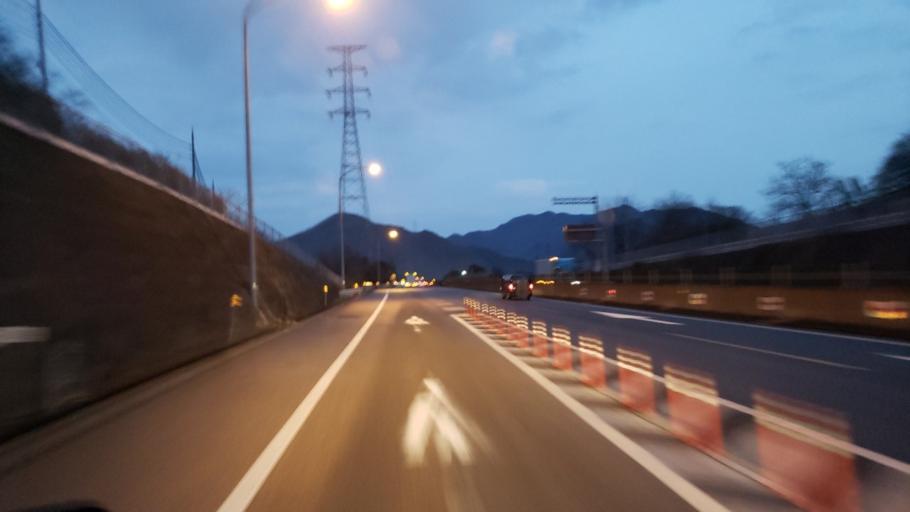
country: JP
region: Hyogo
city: Himeji
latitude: 34.8510
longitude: 134.7440
